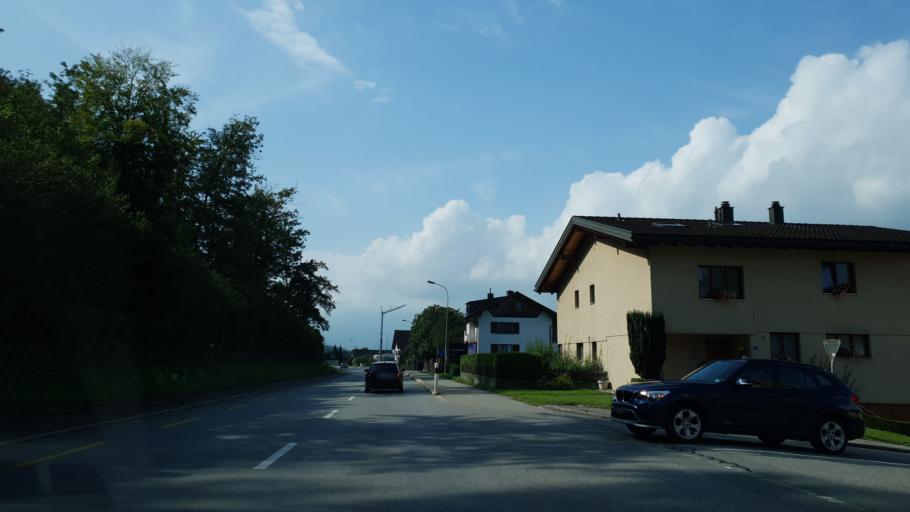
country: LI
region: Mauren
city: Mauren
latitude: 47.2058
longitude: 9.5482
